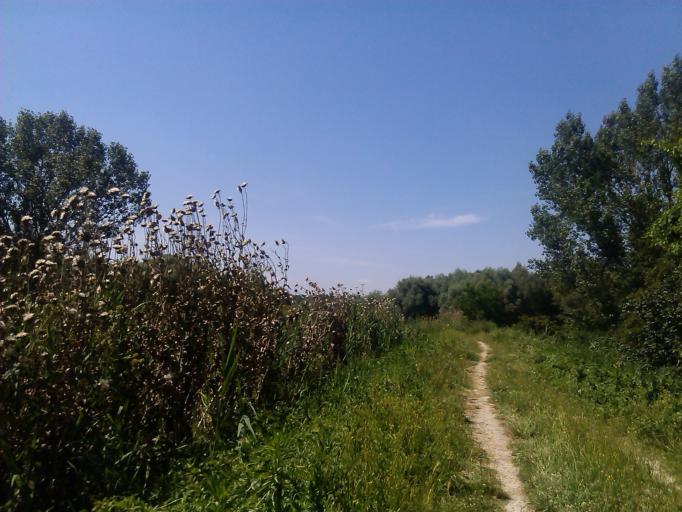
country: IT
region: Umbria
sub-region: Provincia di Perugia
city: Pozzuolo
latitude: 43.0730
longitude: 11.9193
